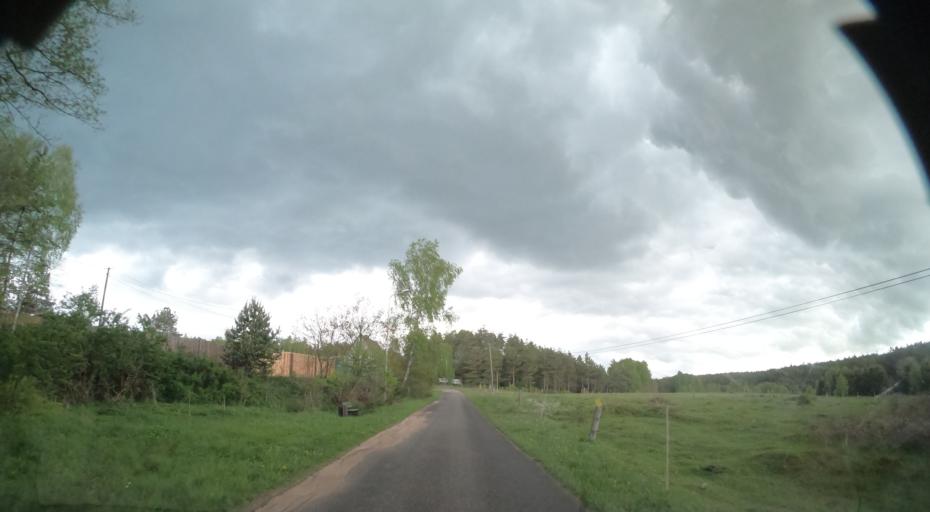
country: PL
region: West Pomeranian Voivodeship
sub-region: Powiat koszalinski
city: Polanow
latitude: 54.1167
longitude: 16.5012
